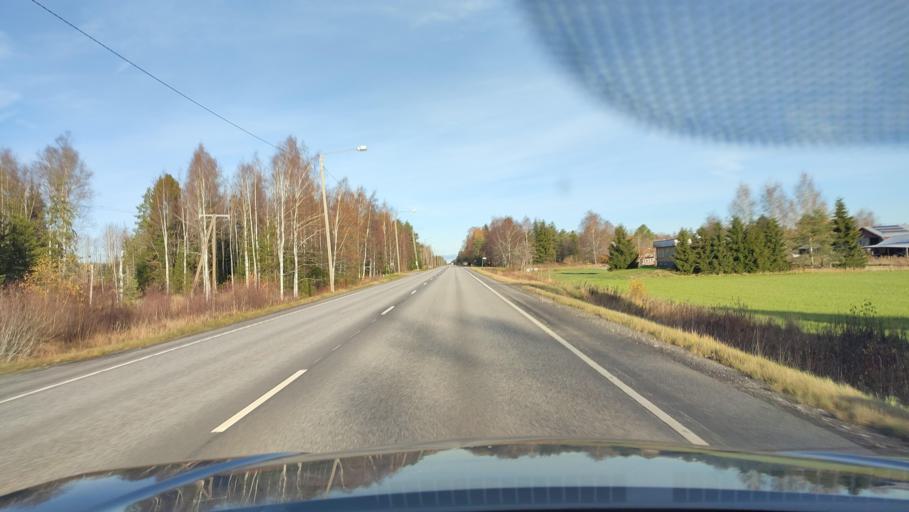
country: FI
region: Ostrobothnia
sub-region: Vaasa
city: Malax
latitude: 62.7761
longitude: 21.6613
